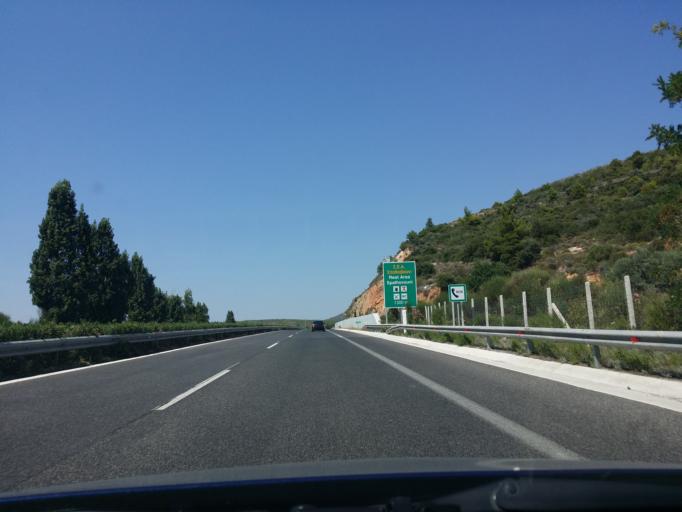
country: GR
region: Peloponnese
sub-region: Nomos Korinthias
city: Khiliomodhi
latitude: 37.8519
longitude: 22.8299
